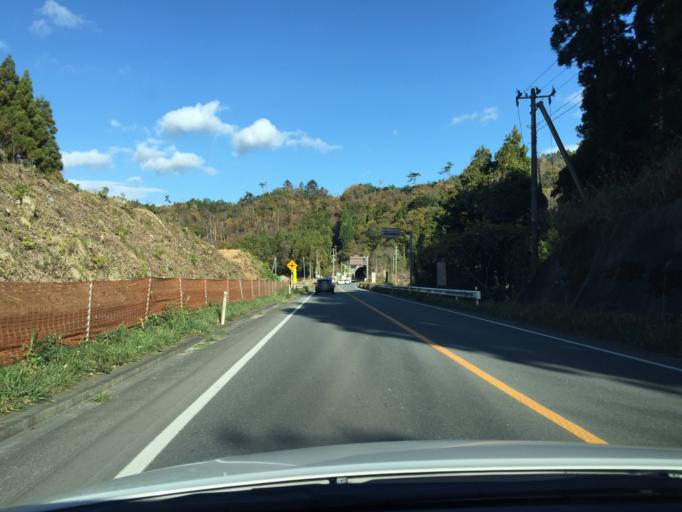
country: JP
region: Fukushima
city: Iwaki
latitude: 37.1589
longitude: 140.9954
